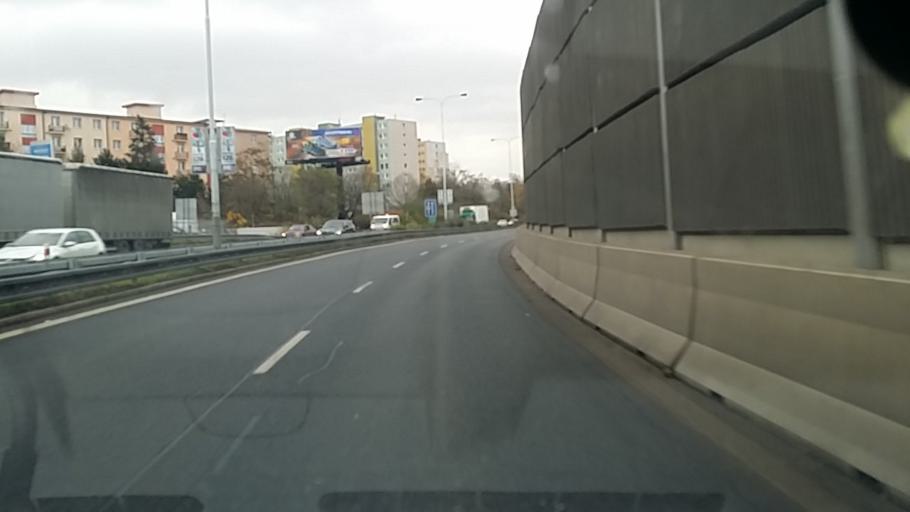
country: CZ
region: Praha
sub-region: Praha 8
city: Karlin
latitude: 50.0493
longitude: 14.4807
